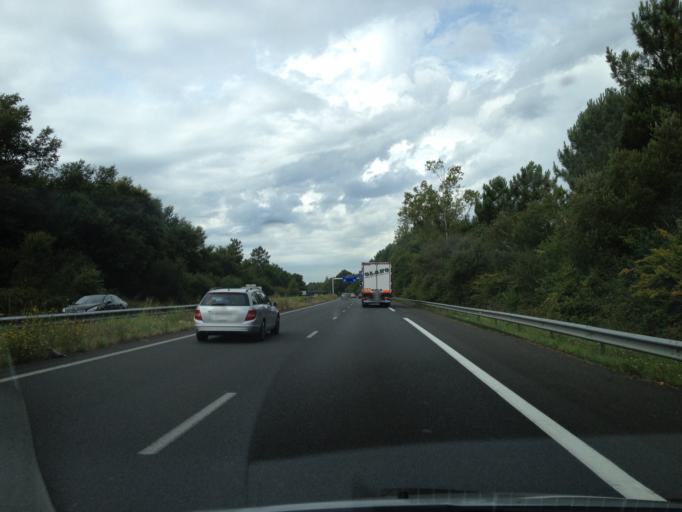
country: FR
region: Aquitaine
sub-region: Departement de la Gironde
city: Castets-en-Dorthe
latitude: 44.5319
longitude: -0.1745
